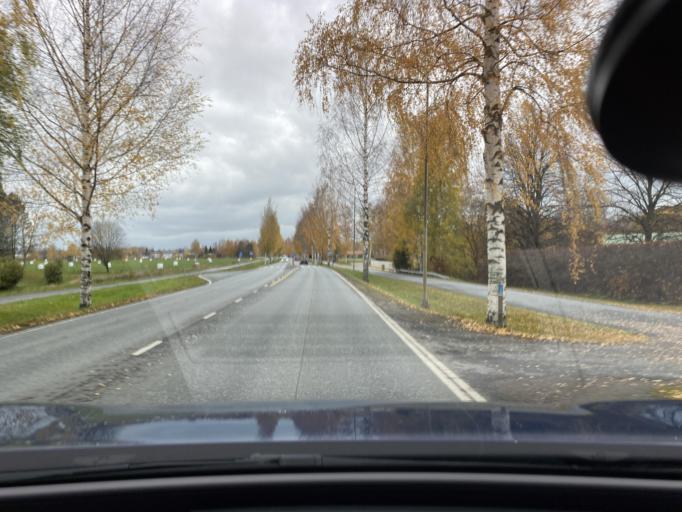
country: FI
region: Satakunta
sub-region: Pori
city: Kokemaeki
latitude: 61.2574
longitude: 22.3380
